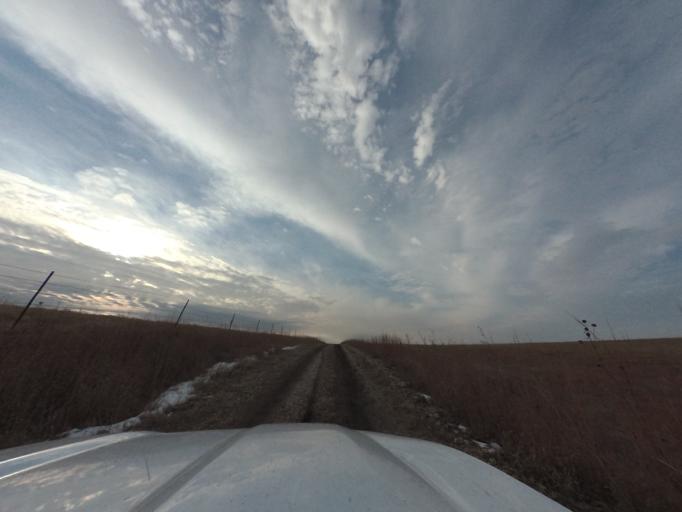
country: US
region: Kansas
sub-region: Chase County
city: Cottonwood Falls
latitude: 38.4628
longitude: -96.4471
